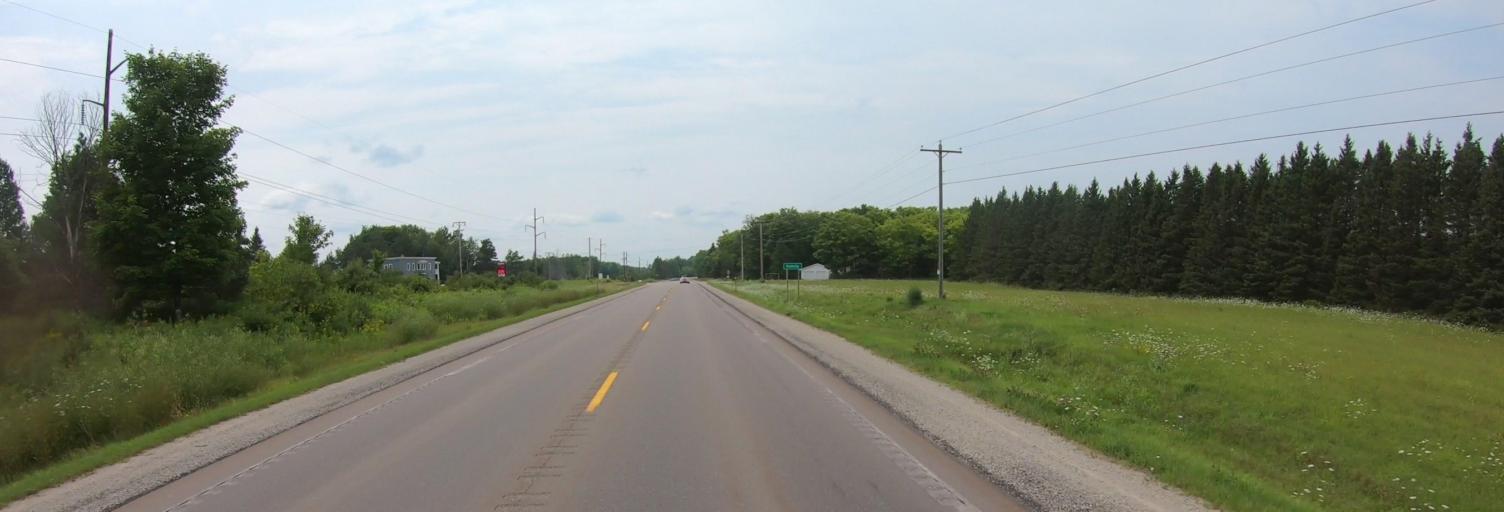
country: US
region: Michigan
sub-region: Marquette County
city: Harvey
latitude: 46.3489
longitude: -87.0307
